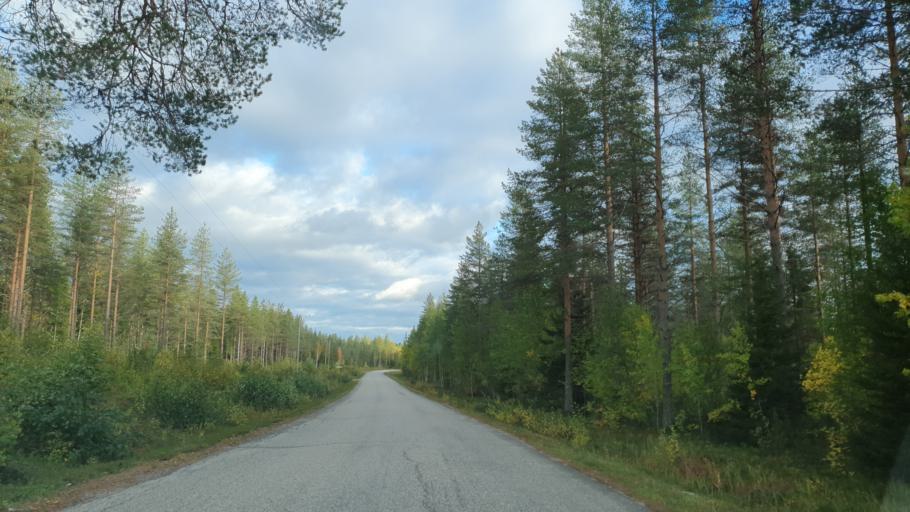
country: FI
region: Kainuu
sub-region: Kehys-Kainuu
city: Kuhmo
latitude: 63.9219
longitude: 30.0472
